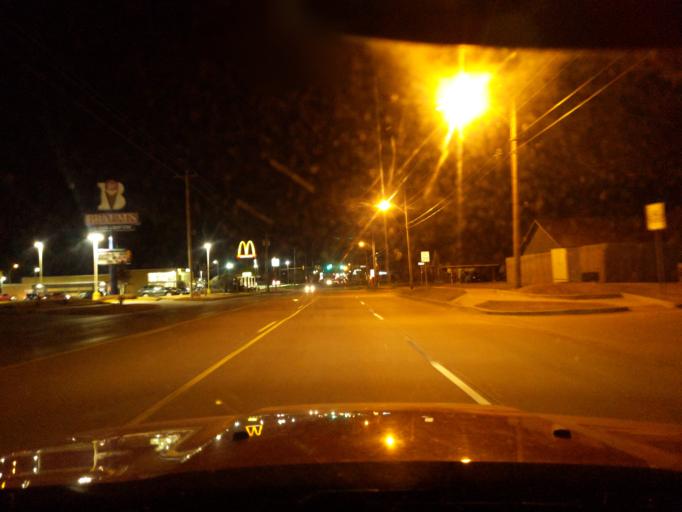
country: US
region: Oklahoma
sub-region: Cleveland County
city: Moore
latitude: 35.3488
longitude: -97.4972
